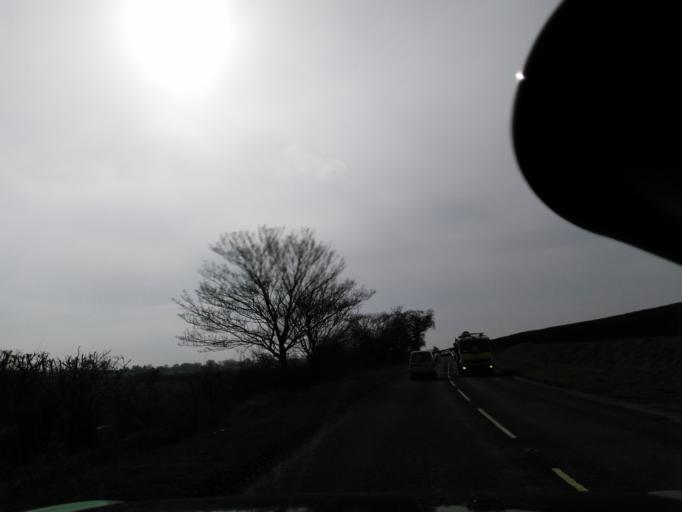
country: GB
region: England
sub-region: North Yorkshire
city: Northallerton
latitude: 54.3156
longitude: -1.4082
